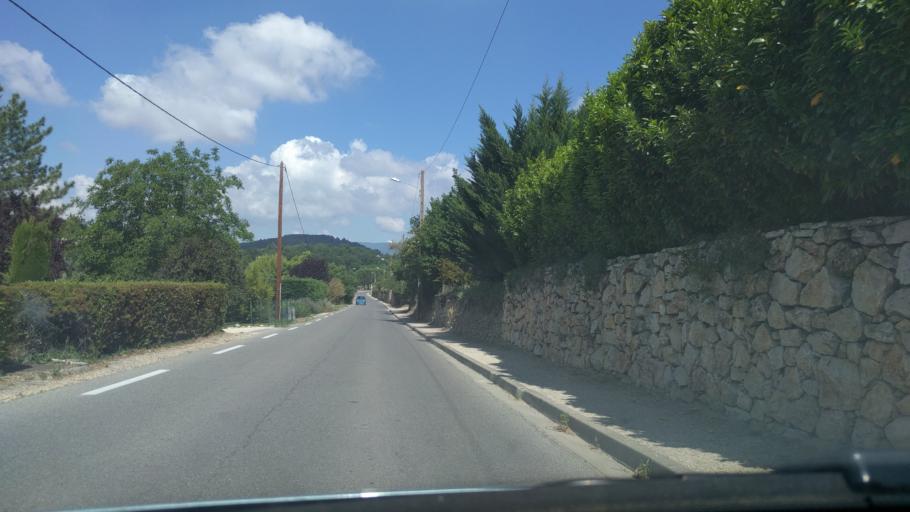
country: FR
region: Provence-Alpes-Cote d'Azur
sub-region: Departement du Vaucluse
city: Grambois
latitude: 43.7295
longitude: 5.5439
